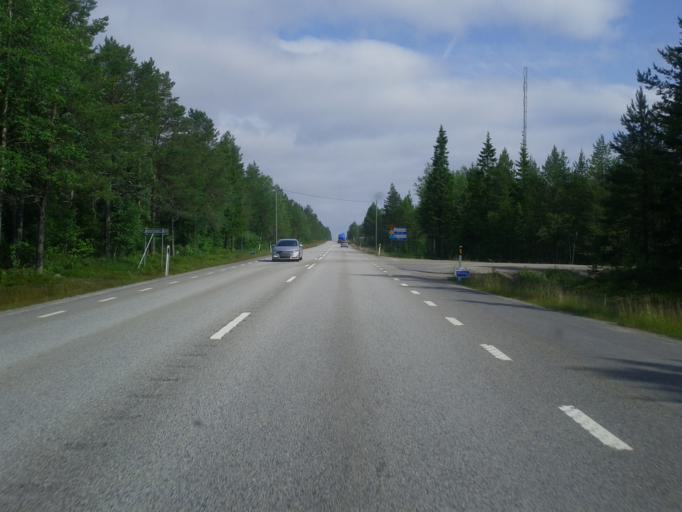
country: SE
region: Vaesterbotten
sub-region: Robertsfors Kommun
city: Robertsfors
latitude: 64.1885
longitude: 20.9971
